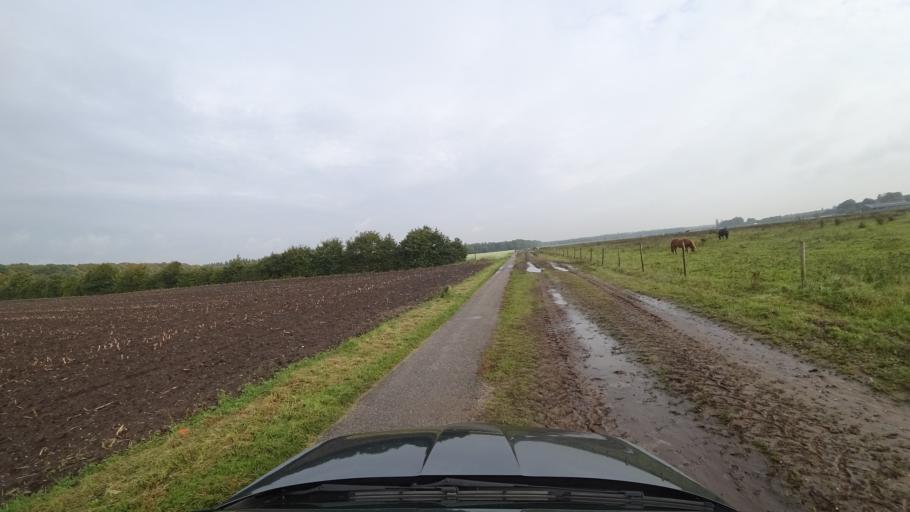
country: NL
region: Gelderland
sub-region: Gemeente Renkum
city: Heelsum
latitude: 51.9927
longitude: 5.7423
